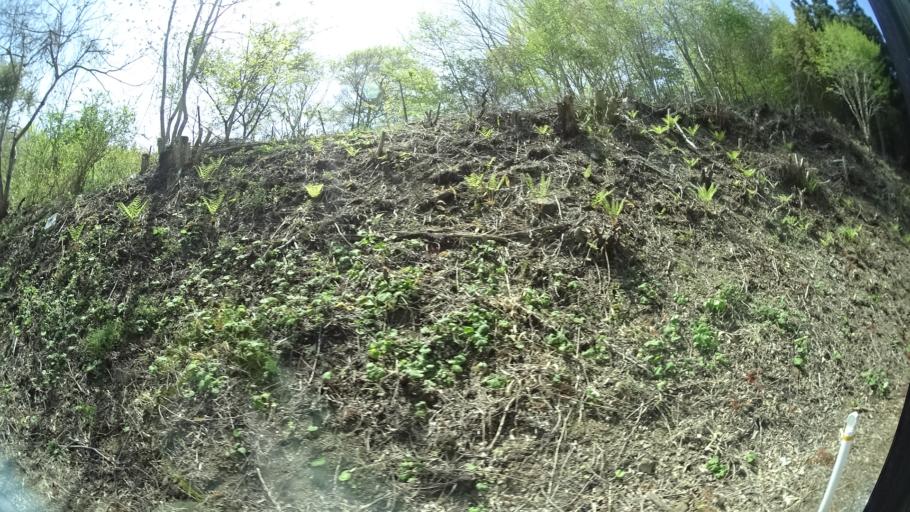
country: JP
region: Iwate
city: Ofunato
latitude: 38.9939
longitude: 141.7102
